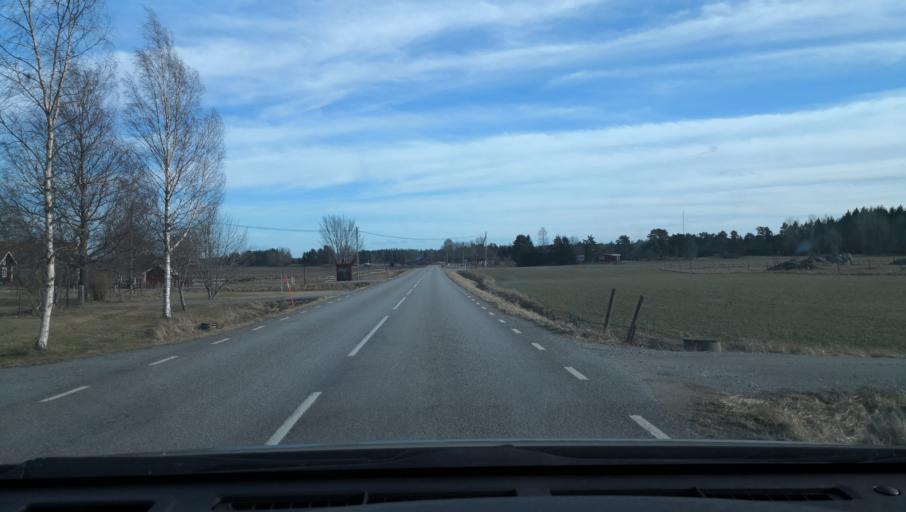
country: SE
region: Uppsala
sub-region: Enkopings Kommun
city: Enkoping
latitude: 59.6054
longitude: 17.1147
